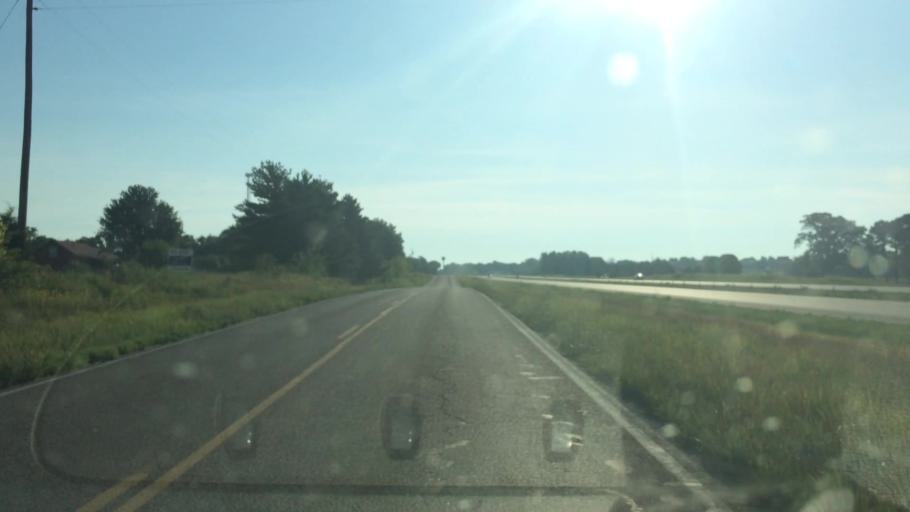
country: US
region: Missouri
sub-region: Greene County
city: Strafford
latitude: 37.2636
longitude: -93.1453
